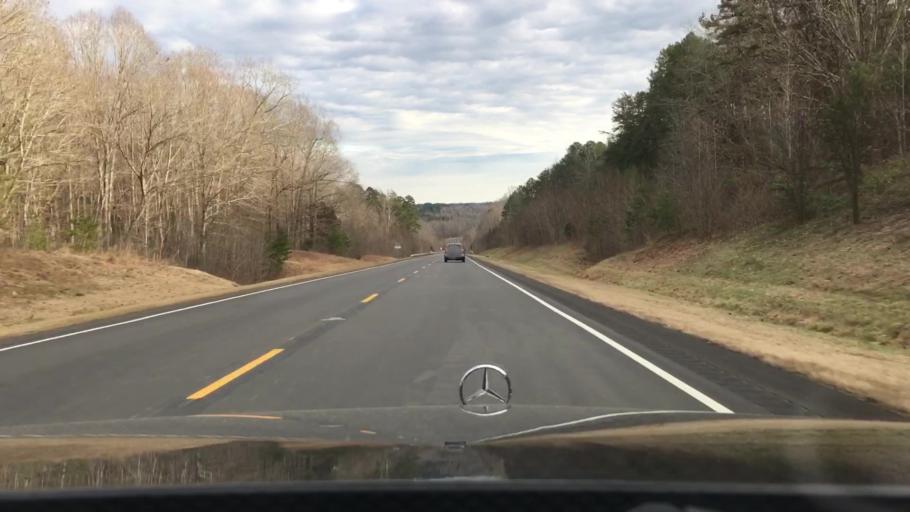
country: US
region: North Carolina
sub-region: Caswell County
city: Yanceyville
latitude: 36.3241
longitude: -79.2345
